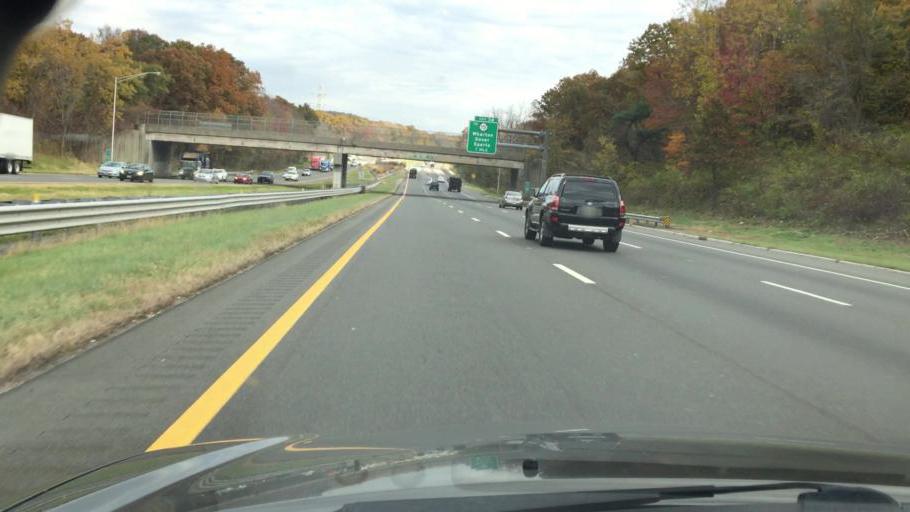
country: US
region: New Jersey
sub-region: Morris County
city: Wharton
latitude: 40.9066
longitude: -74.6035
